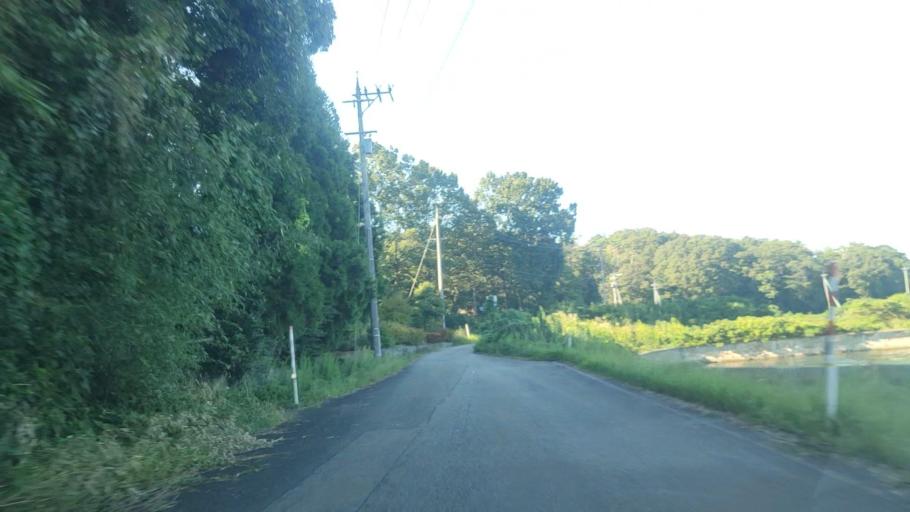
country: JP
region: Ishikawa
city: Nanao
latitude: 37.1225
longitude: 136.8948
